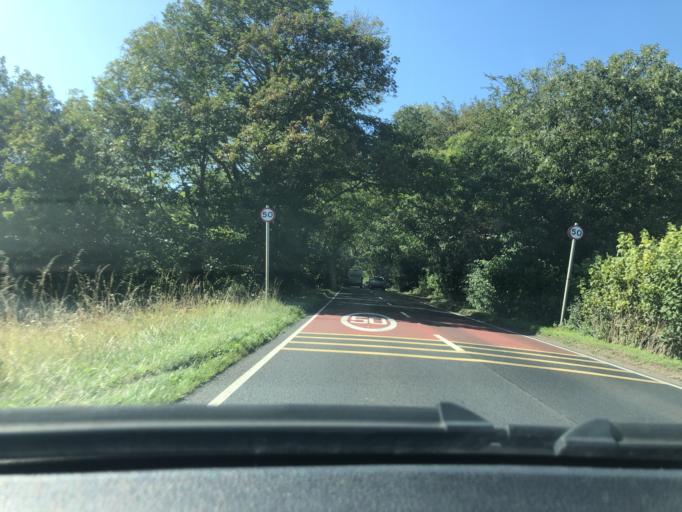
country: GB
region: England
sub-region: Somerset
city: Westonzoyland
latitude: 51.1441
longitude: -2.8899
